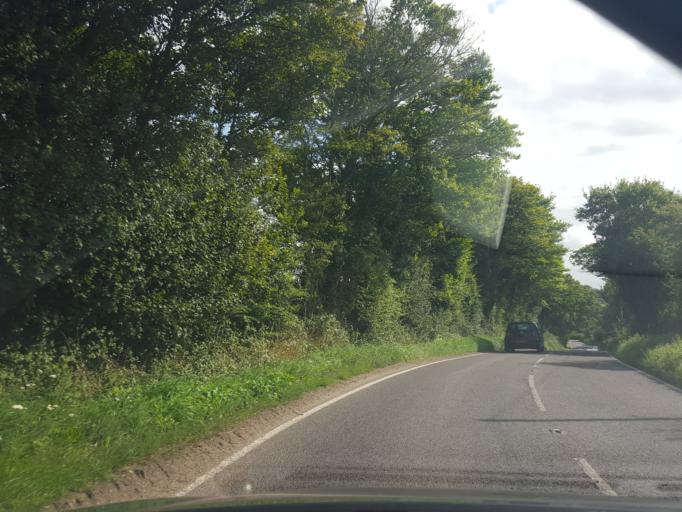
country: GB
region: England
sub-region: Suffolk
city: Shotley Gate
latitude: 51.9341
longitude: 1.2111
